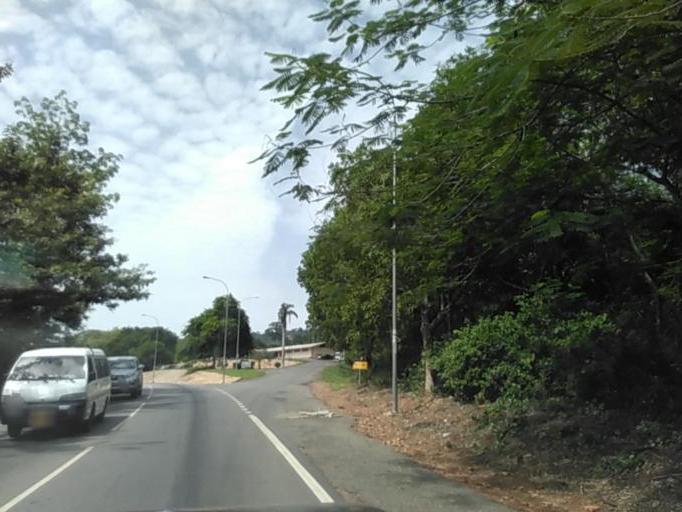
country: GH
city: Akropong
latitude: 6.2659
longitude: 0.0581
